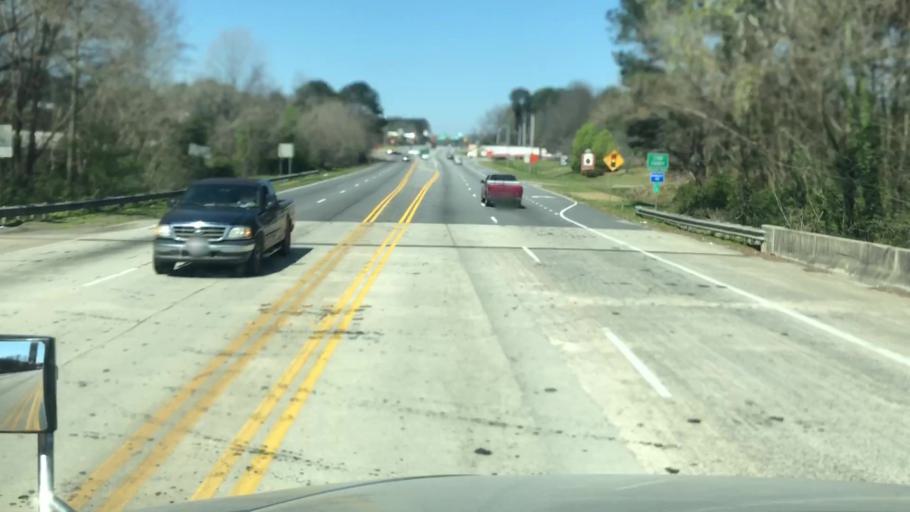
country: US
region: Georgia
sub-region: Cobb County
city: Mableton
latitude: 33.7794
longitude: -84.5339
